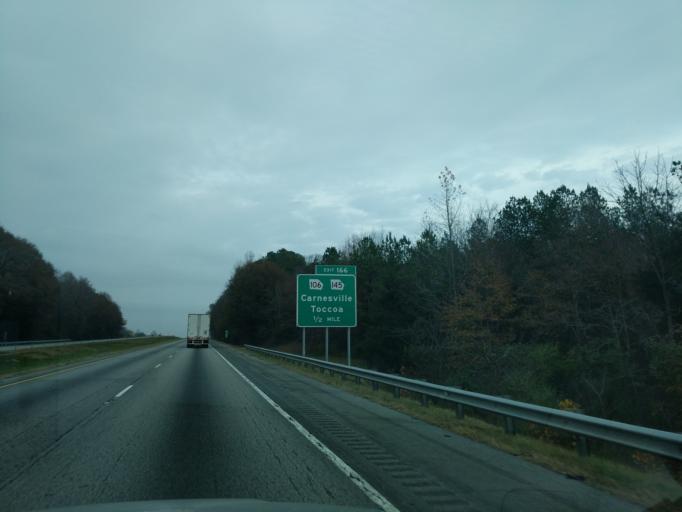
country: US
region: Georgia
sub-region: Franklin County
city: Carnesville
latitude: 34.3853
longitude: -83.2427
